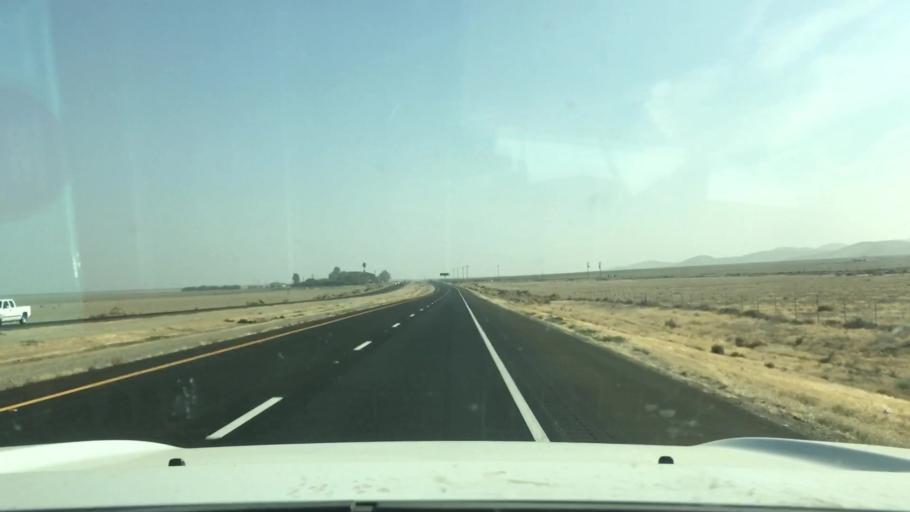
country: US
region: California
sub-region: Kern County
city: Lost Hills
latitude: 35.6437
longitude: -120.0255
